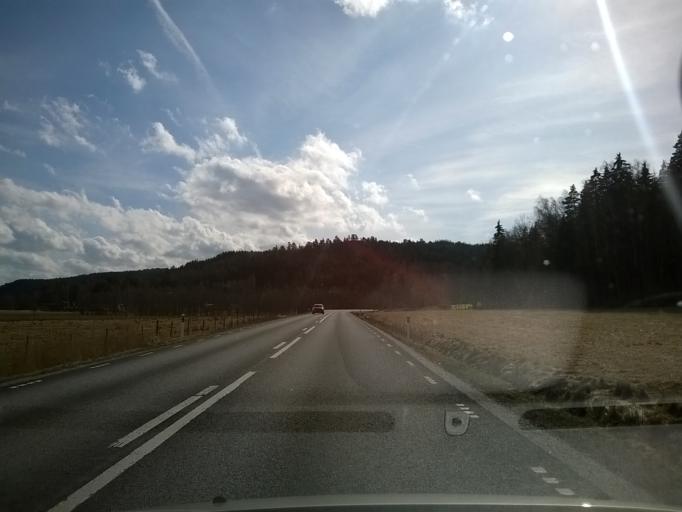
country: SE
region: Vaestra Goetaland
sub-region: Orust
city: Henan
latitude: 58.3387
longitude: 11.6921
